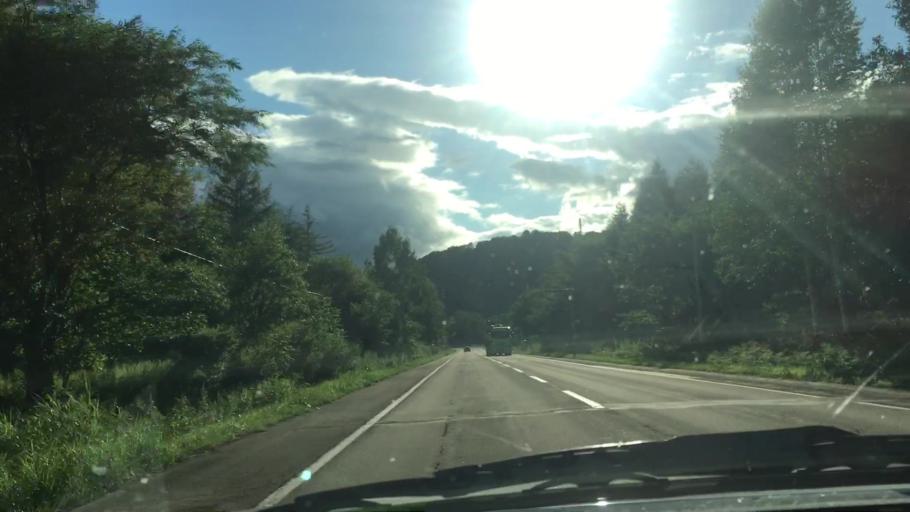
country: JP
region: Hokkaido
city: Shimo-furano
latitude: 43.1307
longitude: 142.6859
